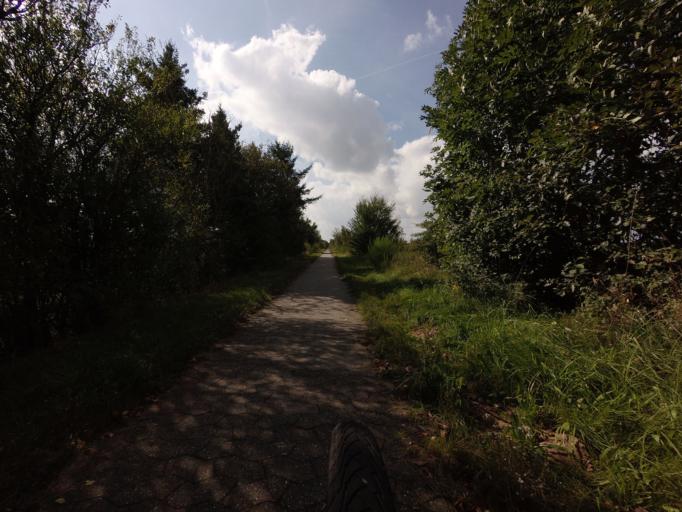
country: DK
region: Central Jutland
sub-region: Viborg Kommune
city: Karup
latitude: 56.3301
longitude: 9.2299
